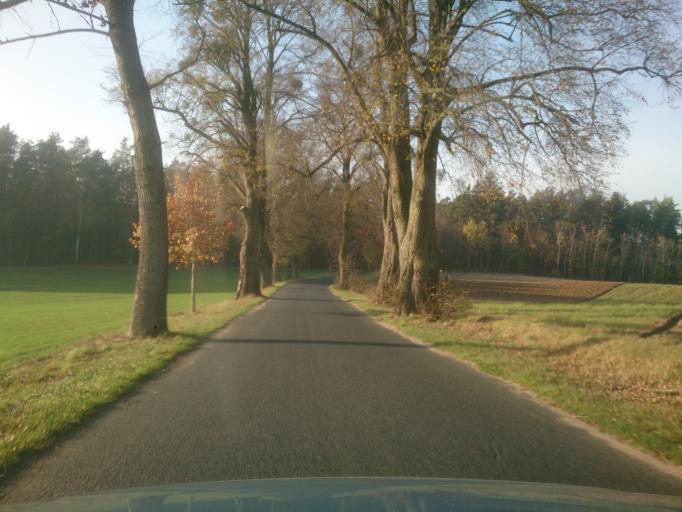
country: PL
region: Kujawsko-Pomorskie
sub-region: Powiat brodnicki
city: Brodnica
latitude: 53.3335
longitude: 19.4678
